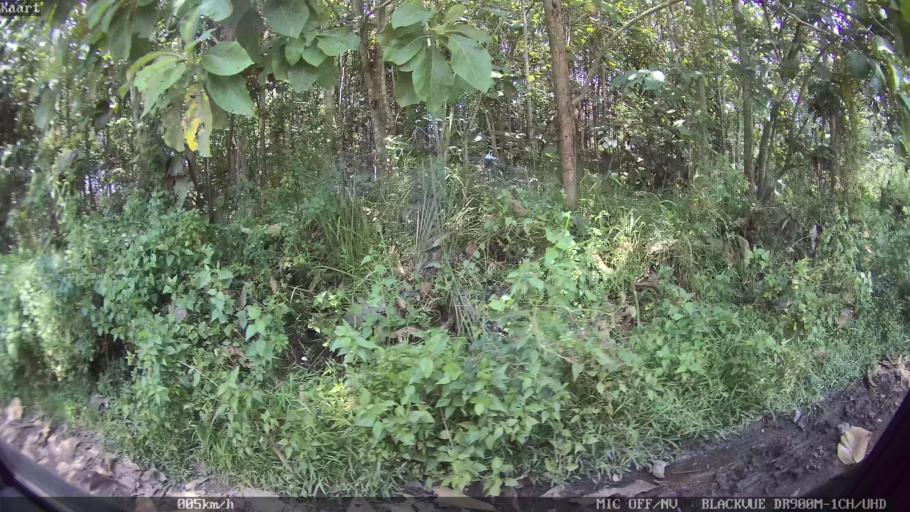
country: ID
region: Lampung
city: Natar
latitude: -5.3156
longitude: 105.2451
